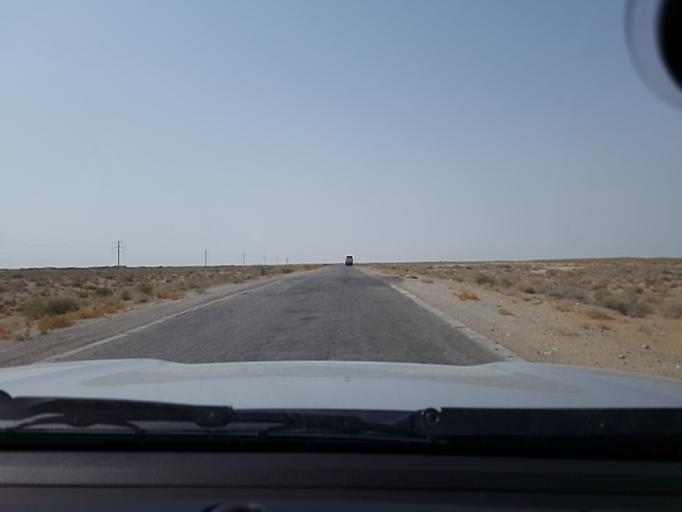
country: TM
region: Balkan
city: Gumdag
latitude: 38.8033
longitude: 54.5983
